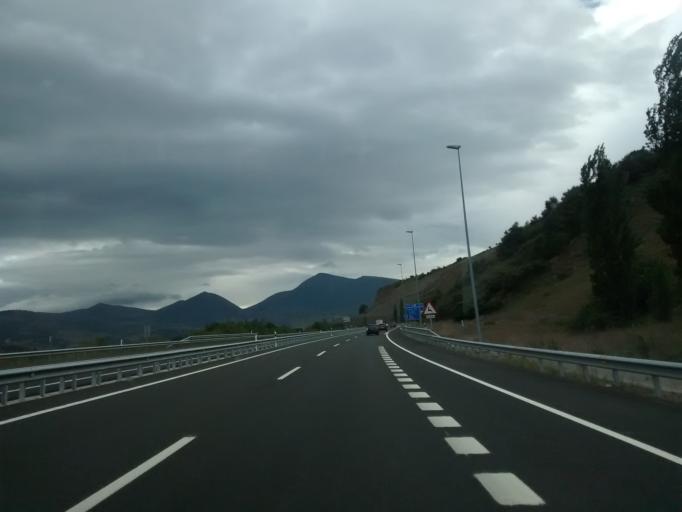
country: ES
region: Cantabria
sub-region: Provincia de Cantabria
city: Arenas de Iguna
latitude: 43.1811
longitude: -4.0575
